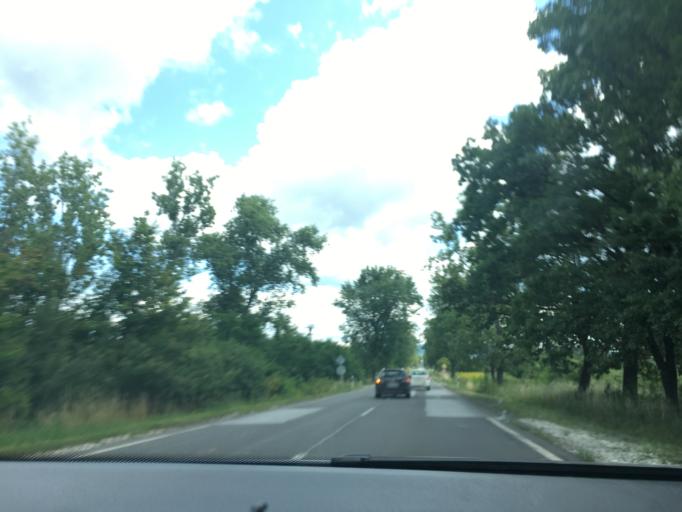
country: HU
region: Borsod-Abauj-Zemplen
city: Olaszliszka
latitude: 48.2191
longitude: 21.3947
